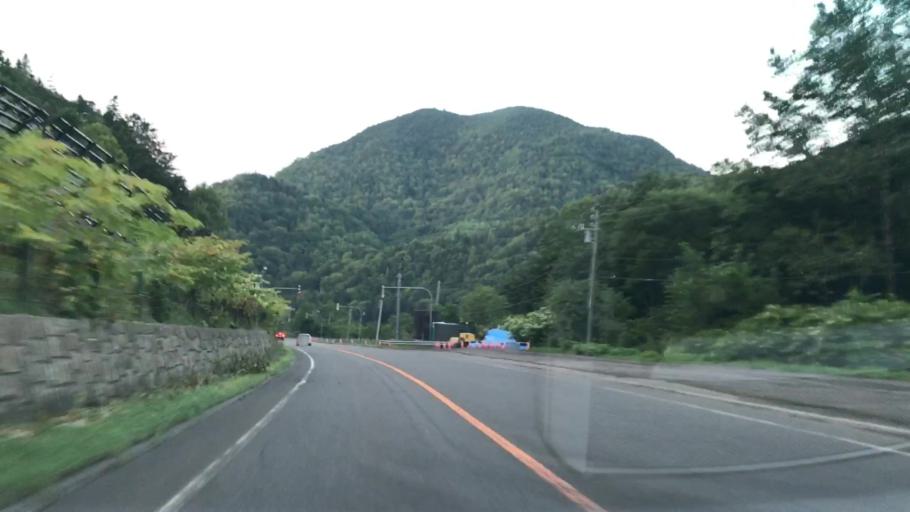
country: JP
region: Hokkaido
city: Sapporo
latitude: 42.9157
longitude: 141.1240
